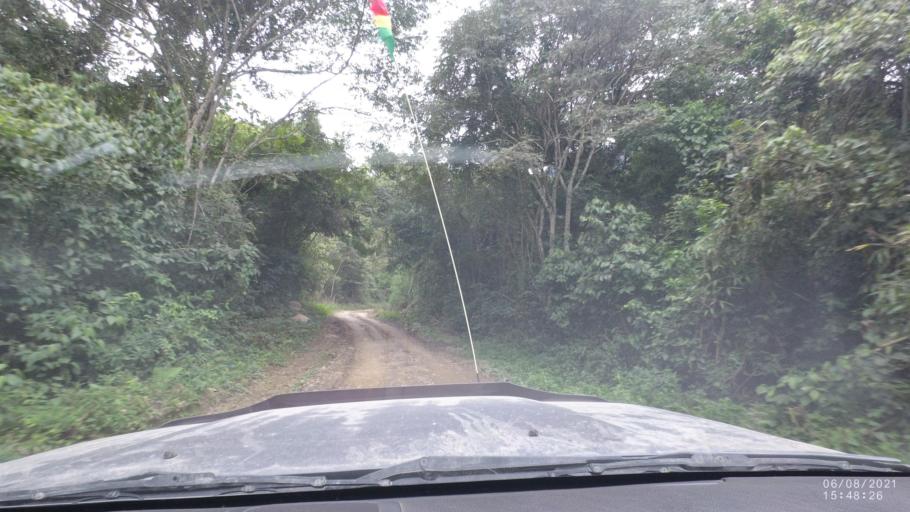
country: BO
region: La Paz
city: Quime
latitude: -16.5909
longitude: -66.7035
